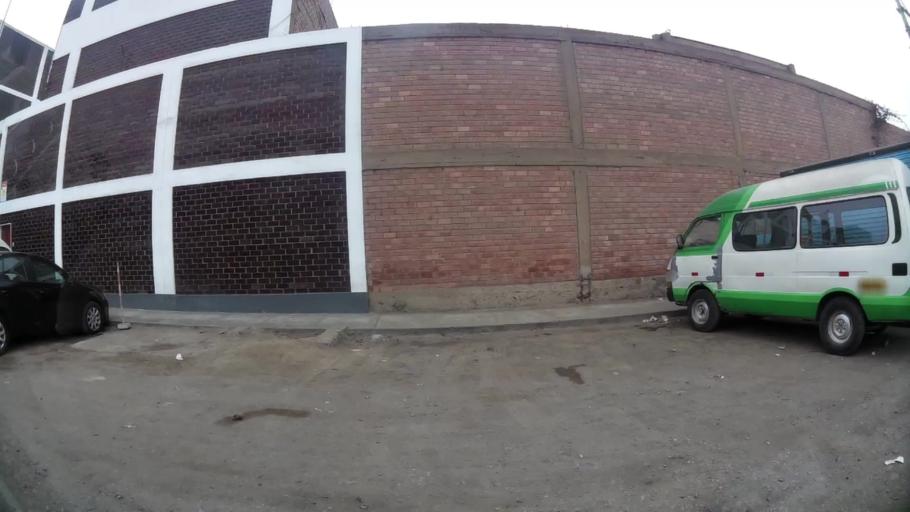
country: PE
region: Lima
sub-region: Lima
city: Surco
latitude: -12.1567
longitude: -76.9809
